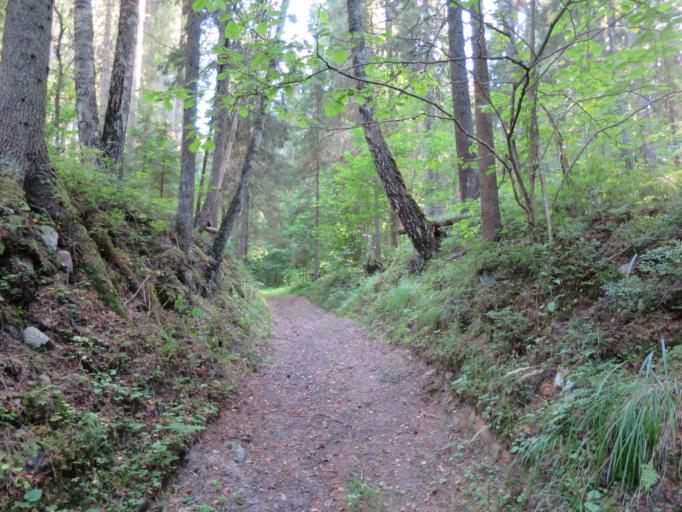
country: LV
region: Ligatne
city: Ligatne
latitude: 57.1283
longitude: 25.1612
